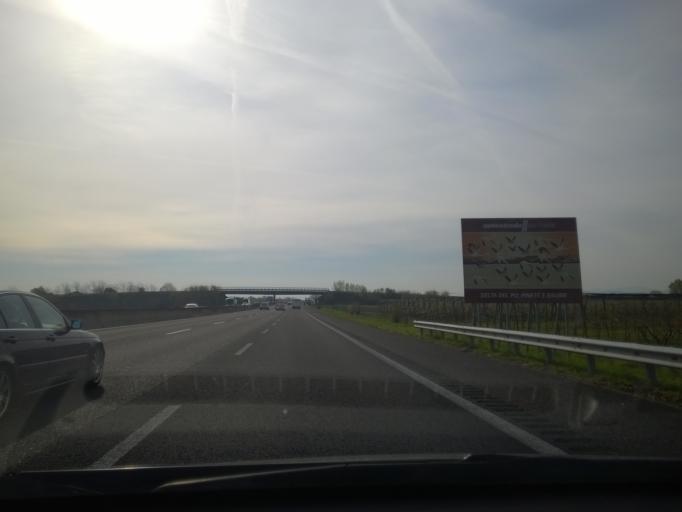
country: IT
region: Emilia-Romagna
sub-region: Forli-Cesena
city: Forlimpopoli
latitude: 44.2346
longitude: 12.1377
